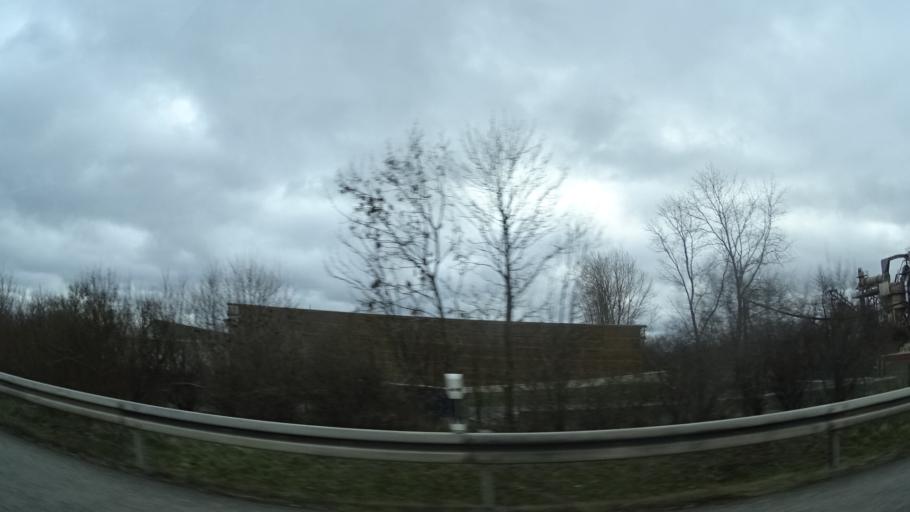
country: DE
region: Thuringia
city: Hetschburg
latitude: 50.9445
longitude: 11.2948
